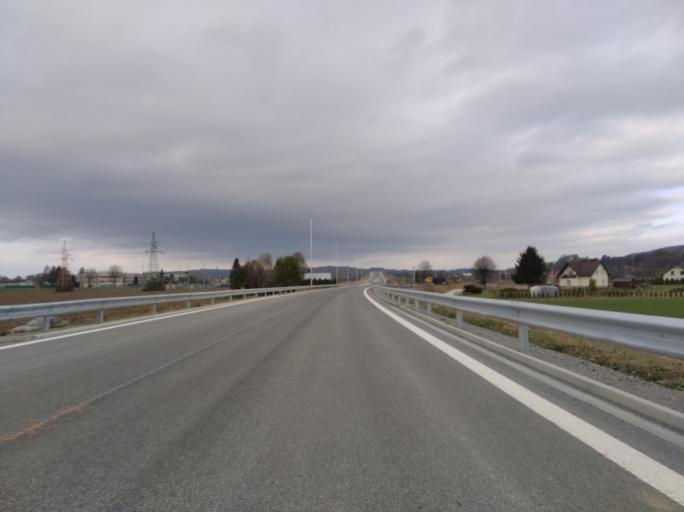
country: PL
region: Subcarpathian Voivodeship
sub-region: Powiat strzyzowski
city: Strzyzow
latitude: 49.8653
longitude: 21.7753
